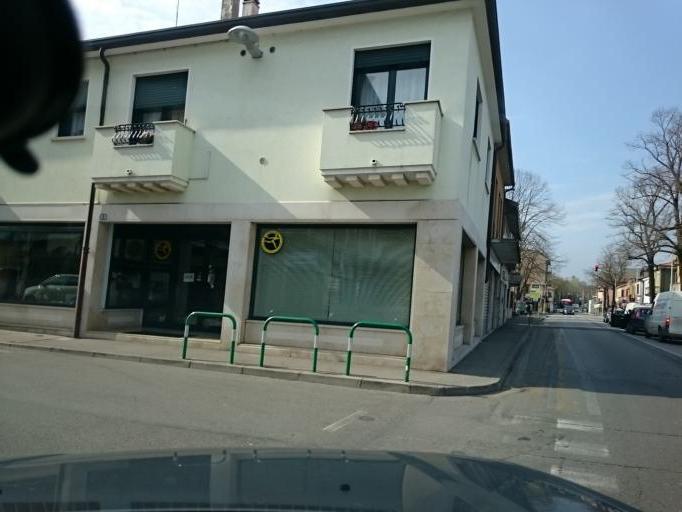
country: IT
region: Veneto
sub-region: Provincia di Padova
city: Ponte San Nicolo
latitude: 45.3795
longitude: 11.9028
